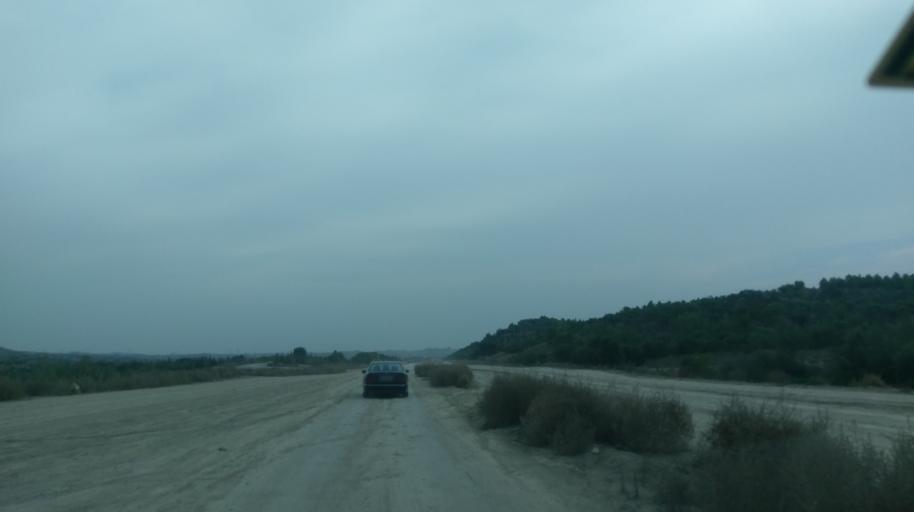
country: CY
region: Lefkosia
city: Nicosia
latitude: 35.2367
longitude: 33.3292
